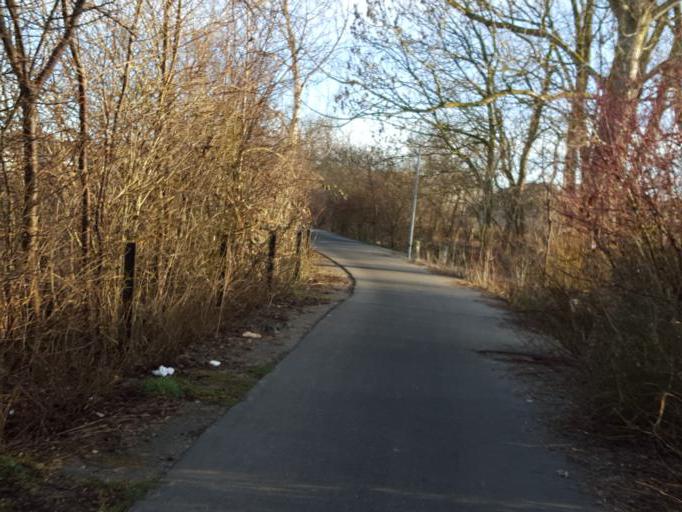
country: DK
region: North Denmark
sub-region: Alborg Kommune
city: Aalborg
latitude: 57.0363
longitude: 9.9179
